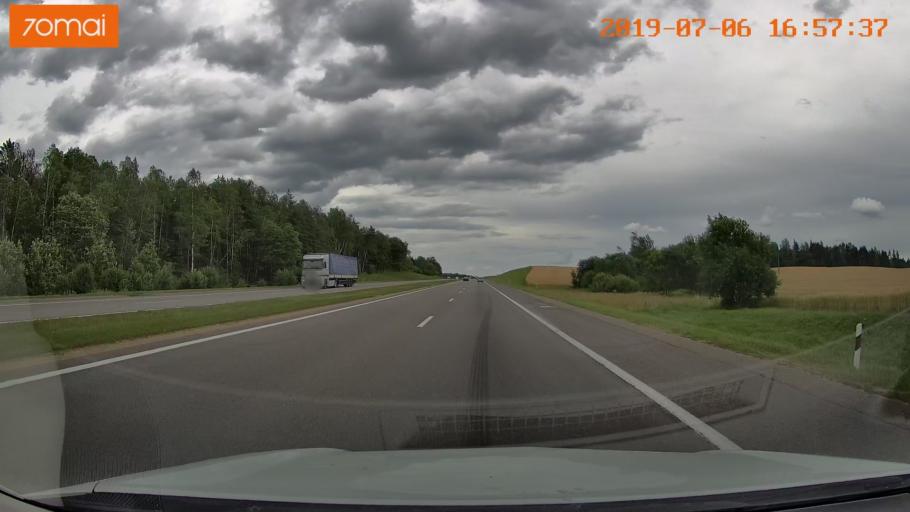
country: BY
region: Minsk
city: Novosel'ye
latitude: 53.9352
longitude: 27.1402
